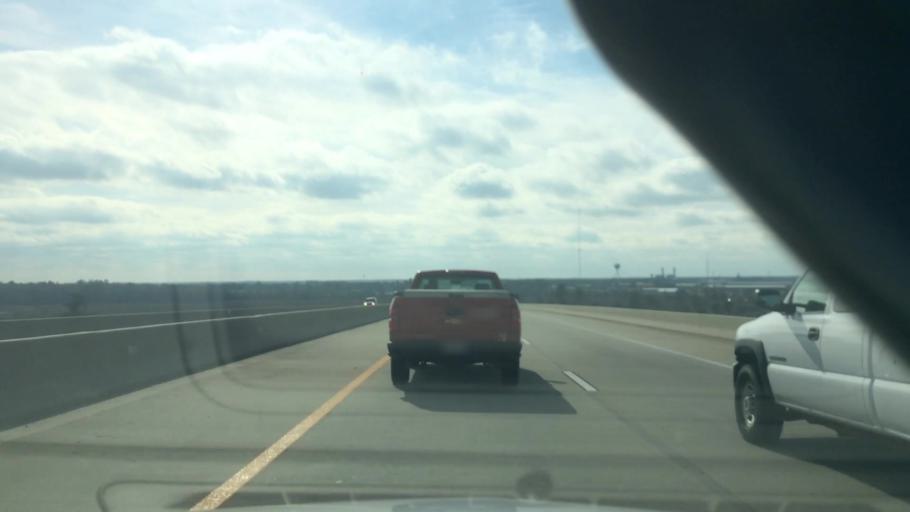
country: US
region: North Carolina
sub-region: New Hanover County
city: Wrightsboro
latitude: 34.2980
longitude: -77.9607
